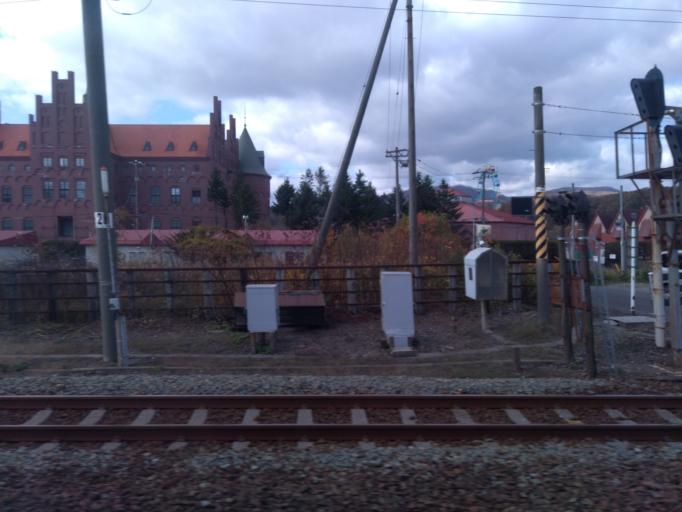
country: JP
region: Hokkaido
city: Shiraoi
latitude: 42.4538
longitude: 141.1839
